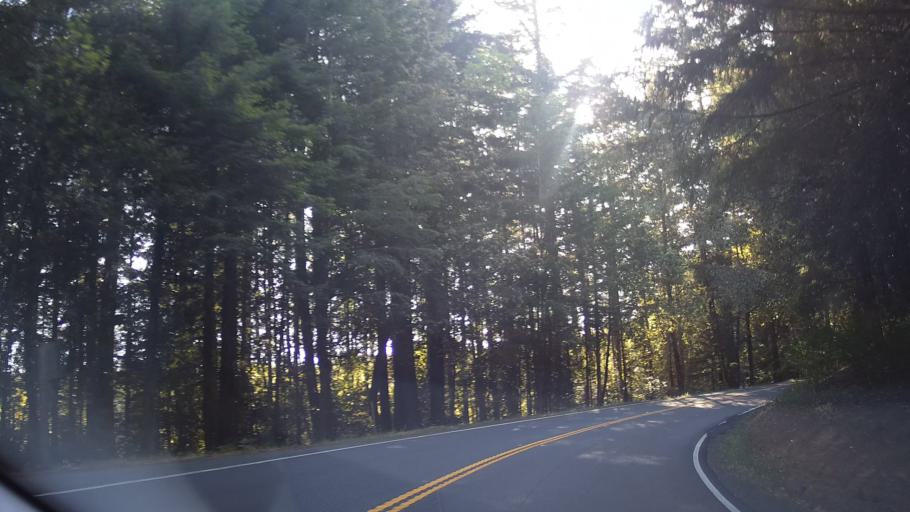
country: US
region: California
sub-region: Mendocino County
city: Fort Bragg
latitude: 39.3558
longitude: -123.6292
